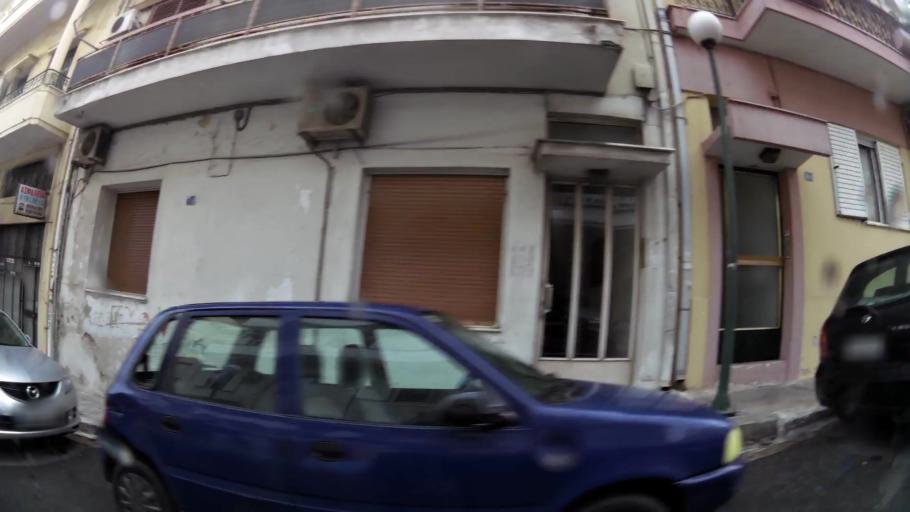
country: GR
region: Attica
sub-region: Nomos Piraios
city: Nikaia
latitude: 37.9588
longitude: 23.6423
